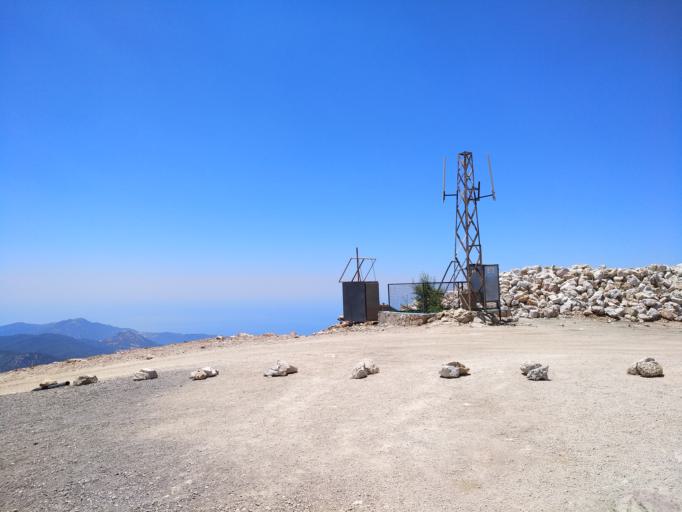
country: TR
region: Mugla
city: OEluedeniz
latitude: 36.5302
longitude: 29.1810
